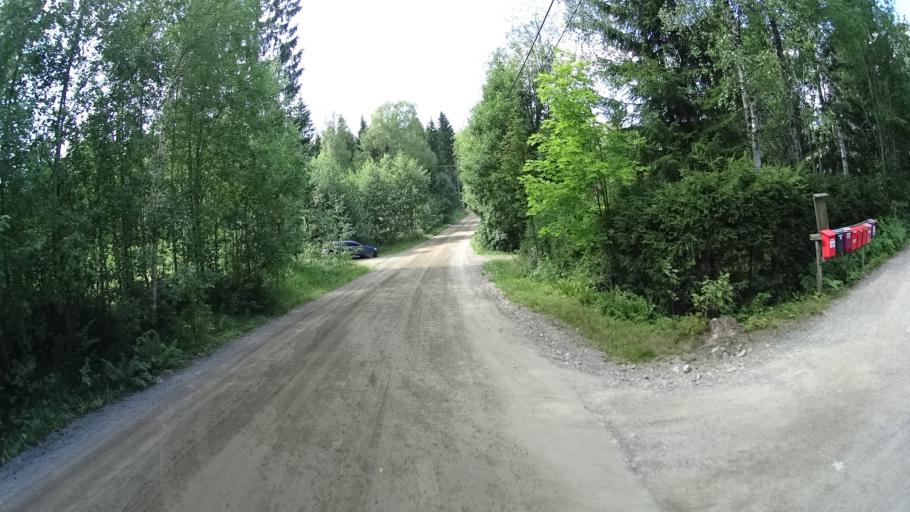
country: FI
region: Uusimaa
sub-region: Porvoo
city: Porvoo
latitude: 60.3935
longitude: 25.7168
